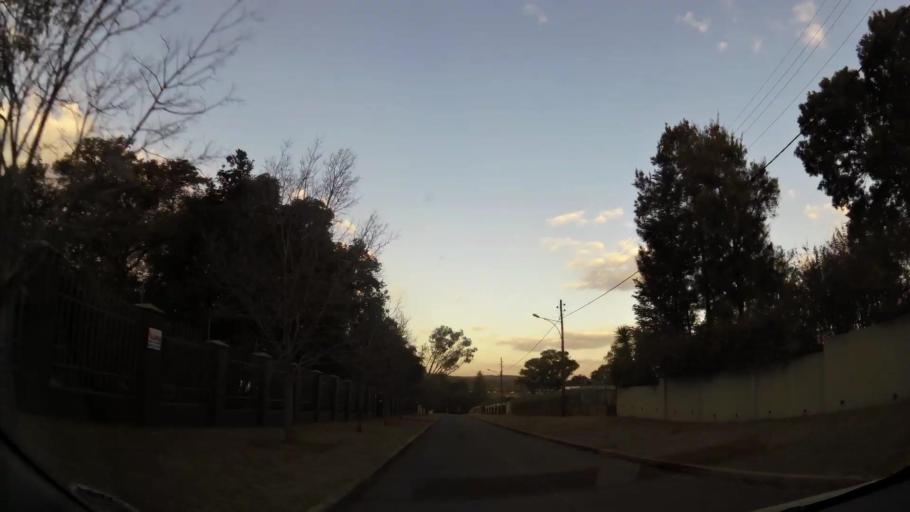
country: ZA
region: Gauteng
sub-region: West Rand District Municipality
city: Krugersdorp
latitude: -26.0668
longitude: 27.7966
